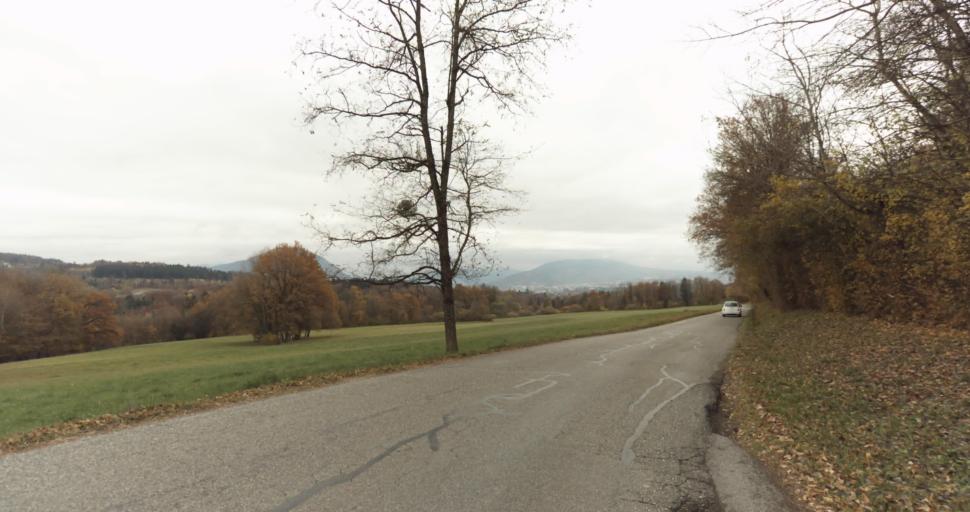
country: FR
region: Rhone-Alpes
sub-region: Departement de la Haute-Savoie
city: Pringy
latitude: 45.9660
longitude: 6.1227
